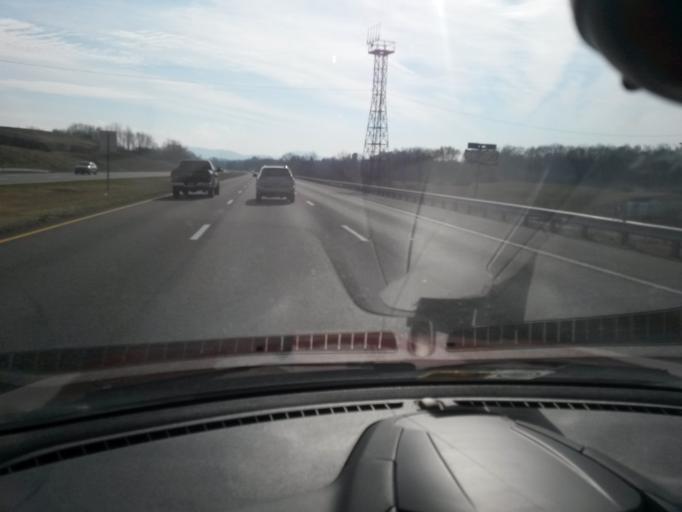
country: US
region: Virginia
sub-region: Roanoke County
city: Hollins
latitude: 37.3219
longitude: -79.9856
